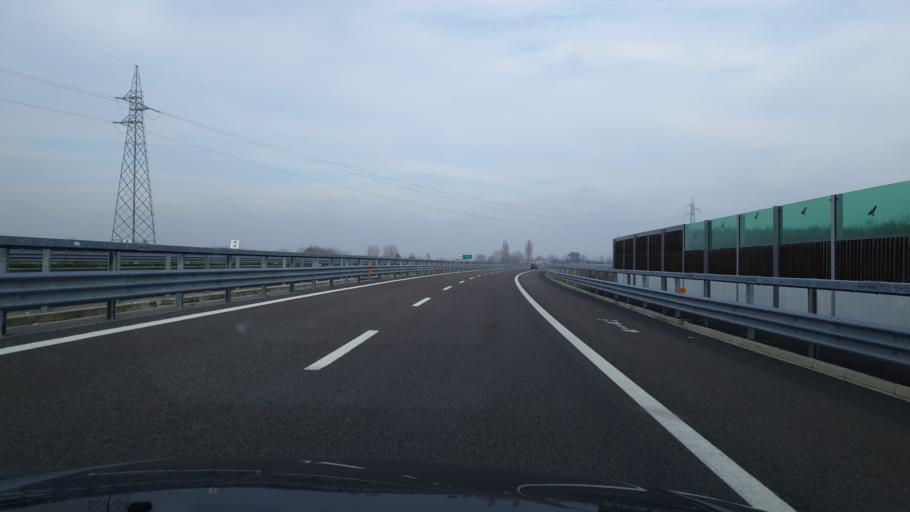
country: IT
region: Veneto
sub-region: Provincia di Padova
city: Saletto
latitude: 45.2321
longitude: 11.5519
